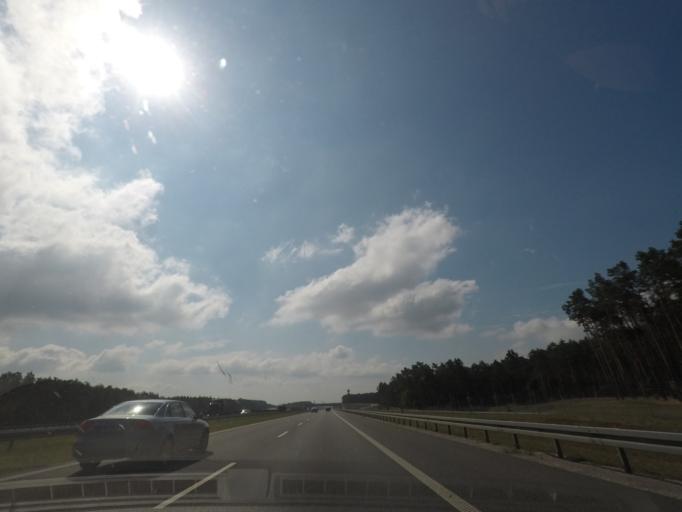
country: PL
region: Kujawsko-Pomorskie
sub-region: Powiat aleksandrowski
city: Aleksandrow Kujawski
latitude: 52.9098
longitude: 18.7181
